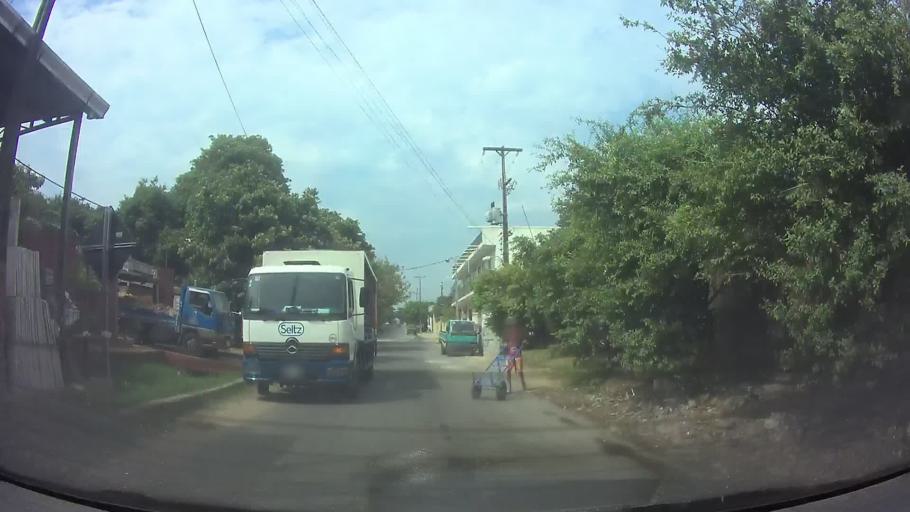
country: PY
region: Central
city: Fernando de la Mora
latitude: -25.2962
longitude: -57.5364
